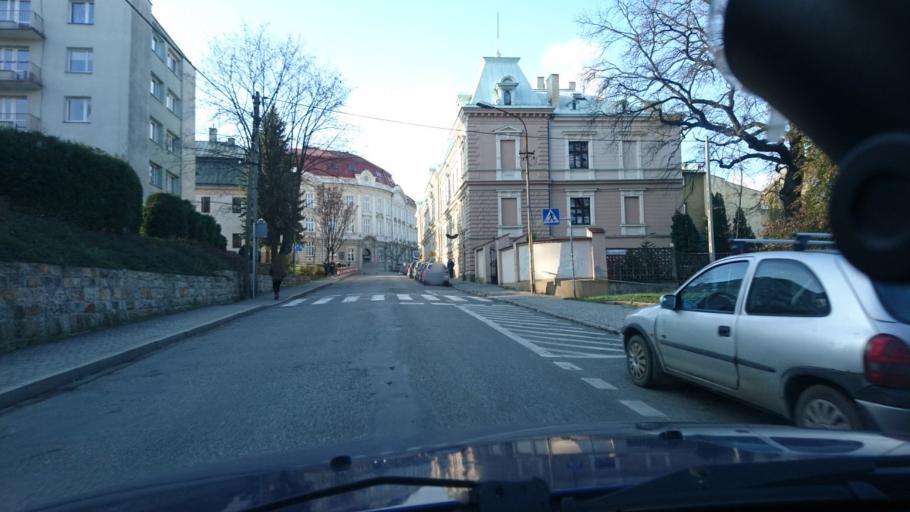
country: PL
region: Silesian Voivodeship
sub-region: Powiat cieszynski
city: Cieszyn
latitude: 49.7497
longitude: 18.6369
